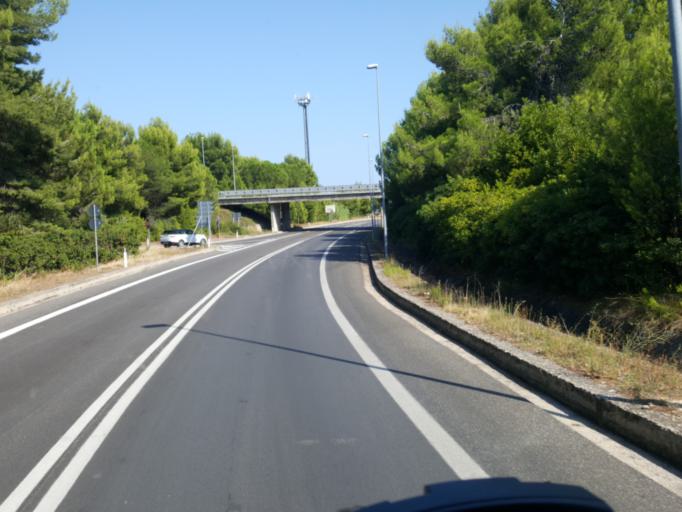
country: IT
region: Abruzzo
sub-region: Provincia di Chieti
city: Salvo Marina
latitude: 42.0604
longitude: 14.7665
